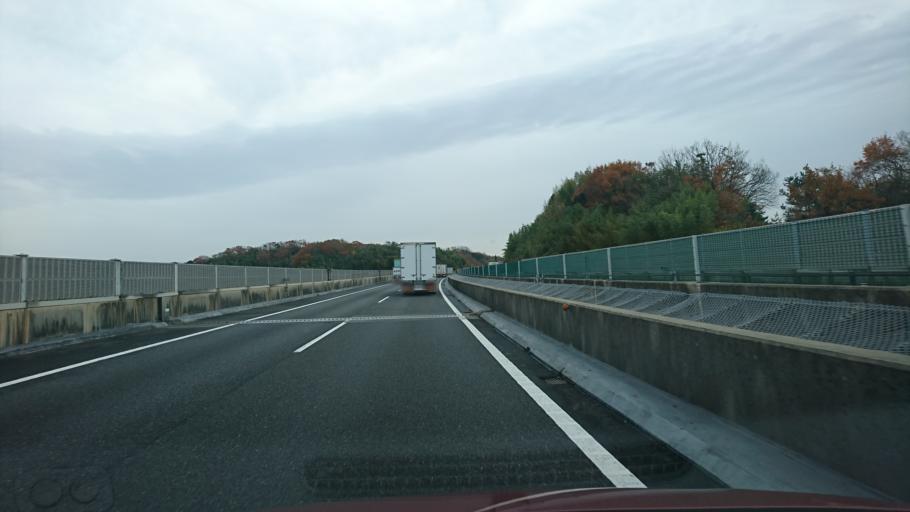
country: JP
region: Hyogo
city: Sandacho
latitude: 34.8313
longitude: 135.1642
